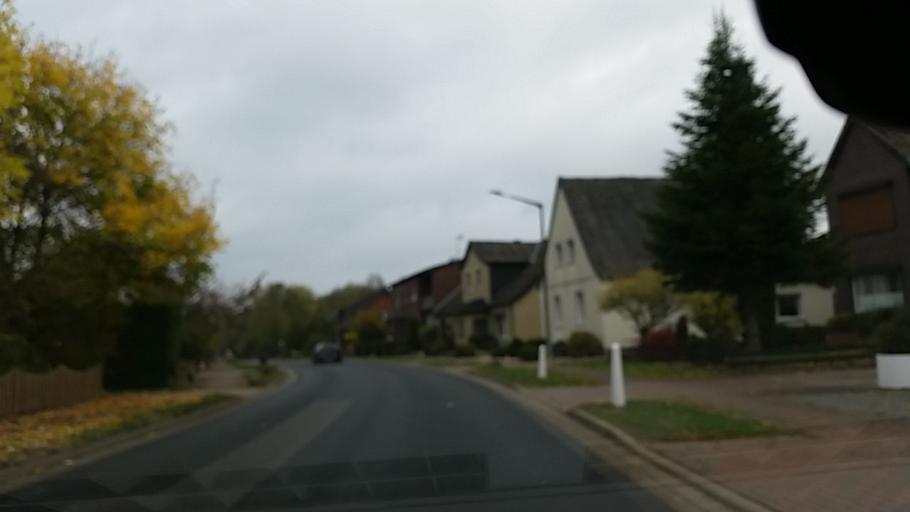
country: DE
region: Lower Saxony
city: Tulau
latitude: 52.6202
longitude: 10.8143
